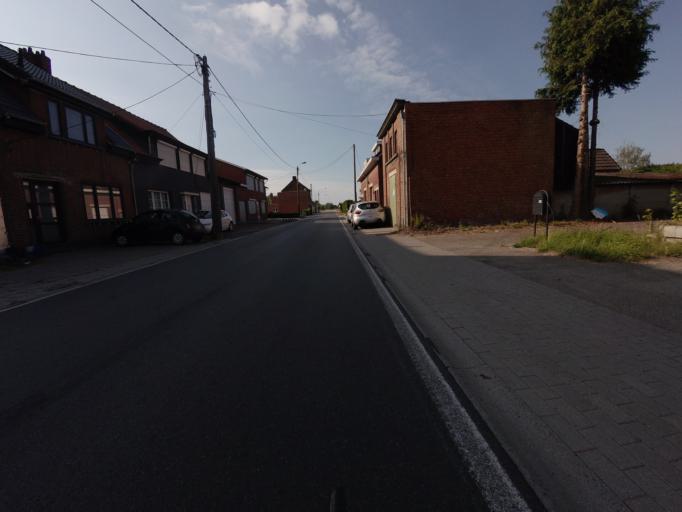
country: BE
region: Flanders
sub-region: Provincie Antwerpen
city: Ranst
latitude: 51.2061
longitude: 4.5977
